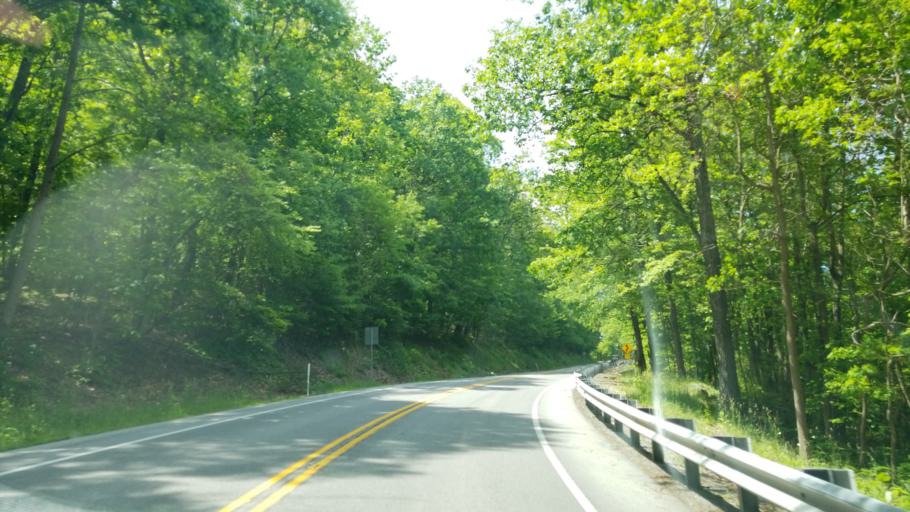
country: US
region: Pennsylvania
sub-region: Blair County
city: Tyrone
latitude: 40.6938
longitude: -78.2801
